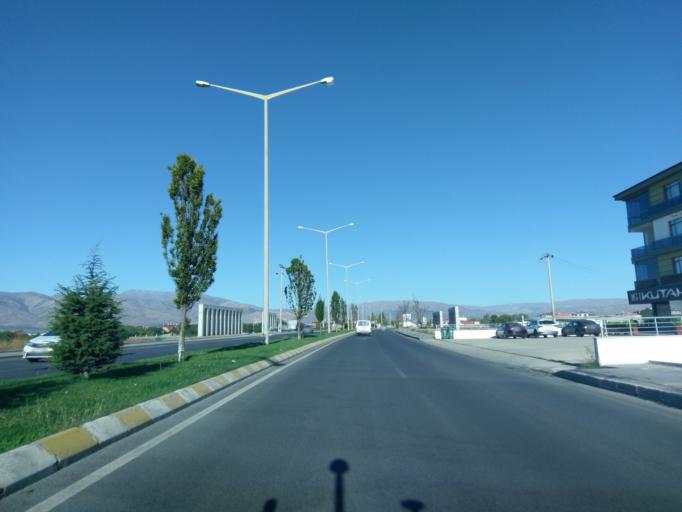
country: TR
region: Erzincan
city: Erzincan
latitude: 39.7494
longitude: 39.4619
